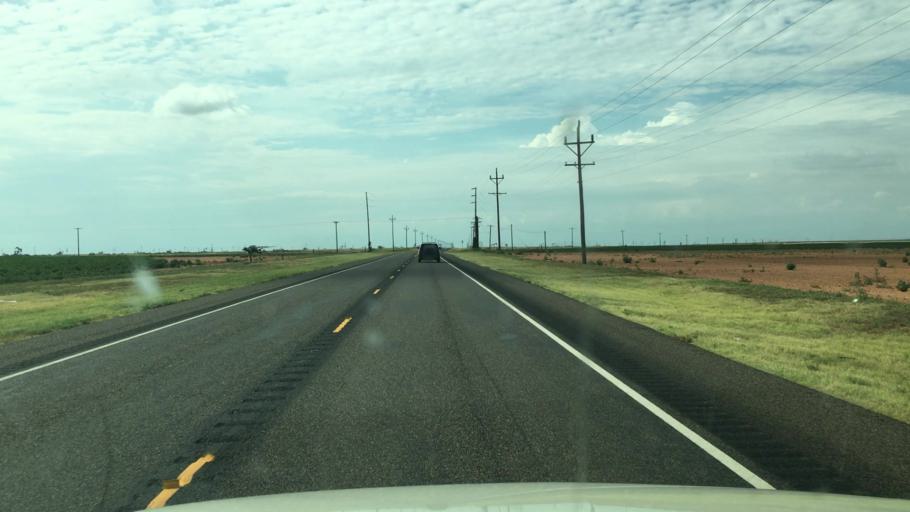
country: US
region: Texas
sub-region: Dawson County
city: Lamesa
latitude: 32.8879
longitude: -102.0876
